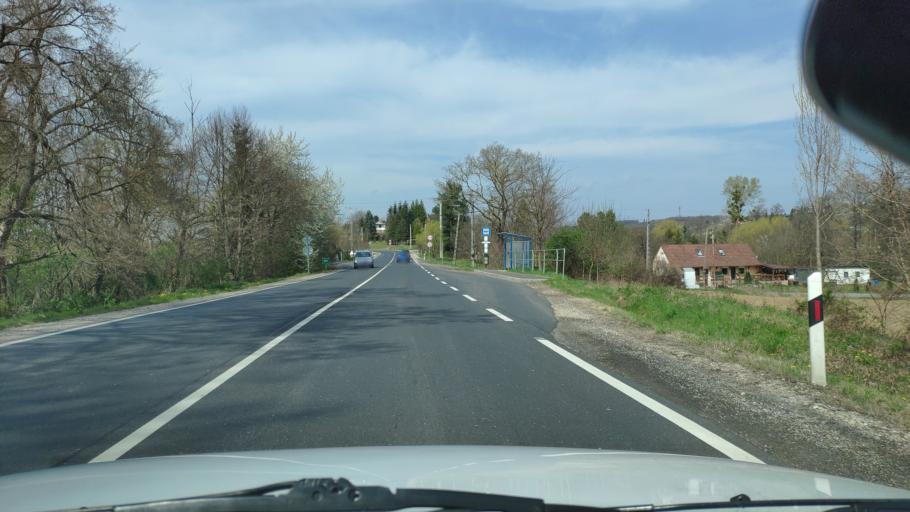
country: HU
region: Zala
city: Nagykanizsa
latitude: 46.4332
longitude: 17.0387
